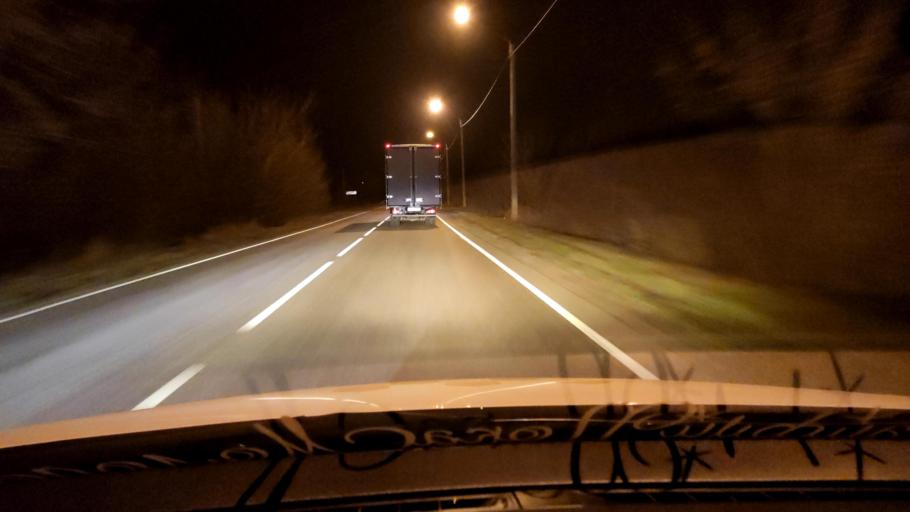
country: RU
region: Voronezj
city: Semiluki
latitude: 51.7753
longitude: 39.0513
